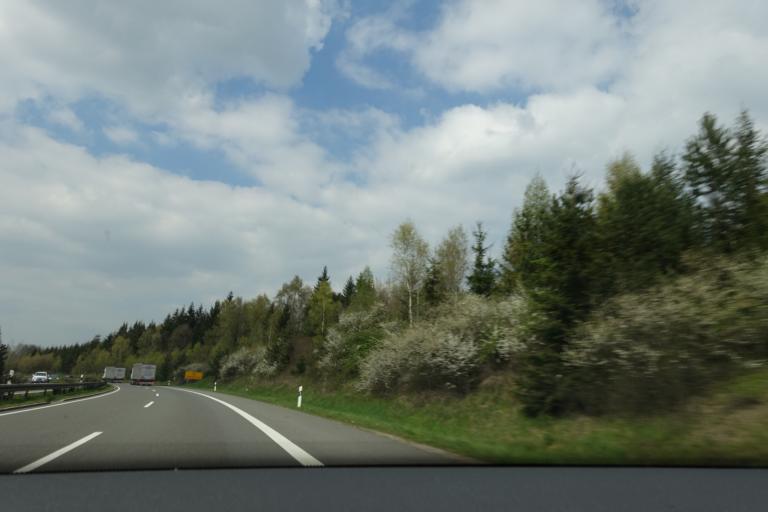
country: DE
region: Saxony
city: Gornau
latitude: 50.7665
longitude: 13.0172
